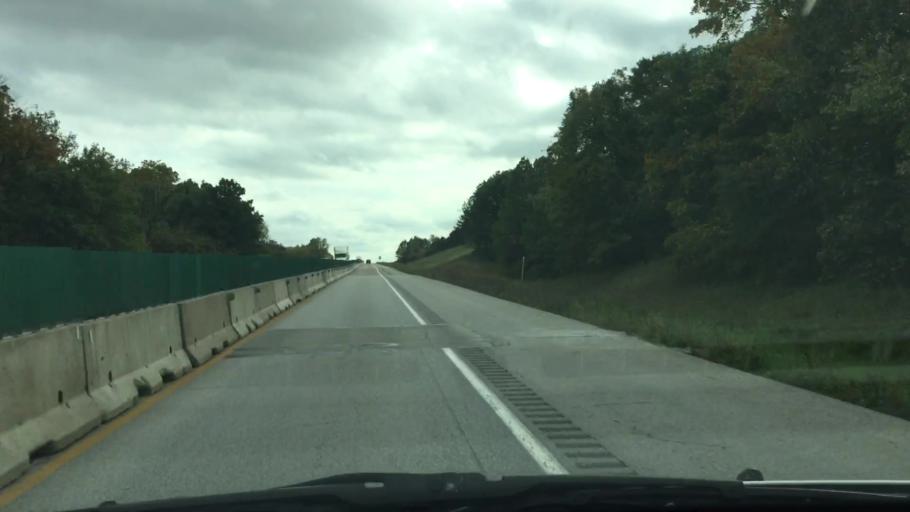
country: US
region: Iowa
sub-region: Decatur County
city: Leon
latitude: 40.6951
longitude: -93.8462
